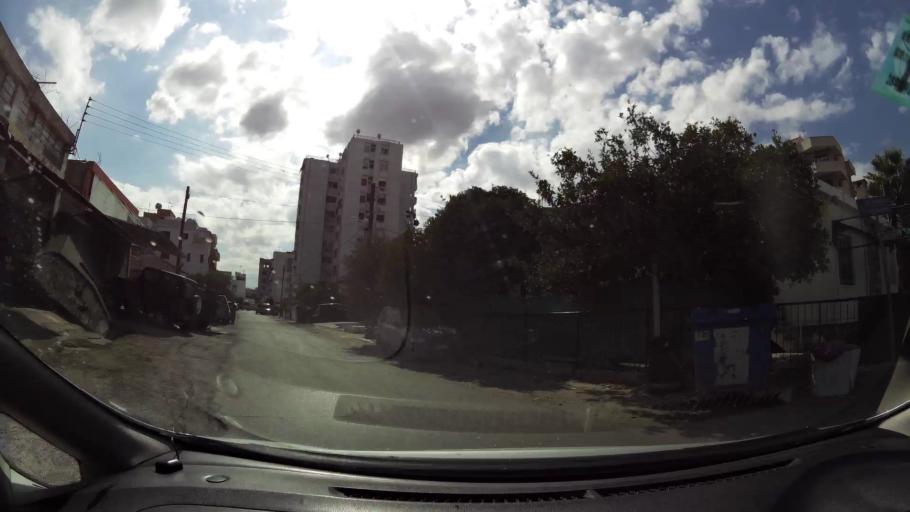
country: CY
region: Lefkosia
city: Nicosia
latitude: 35.1829
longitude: 33.3873
